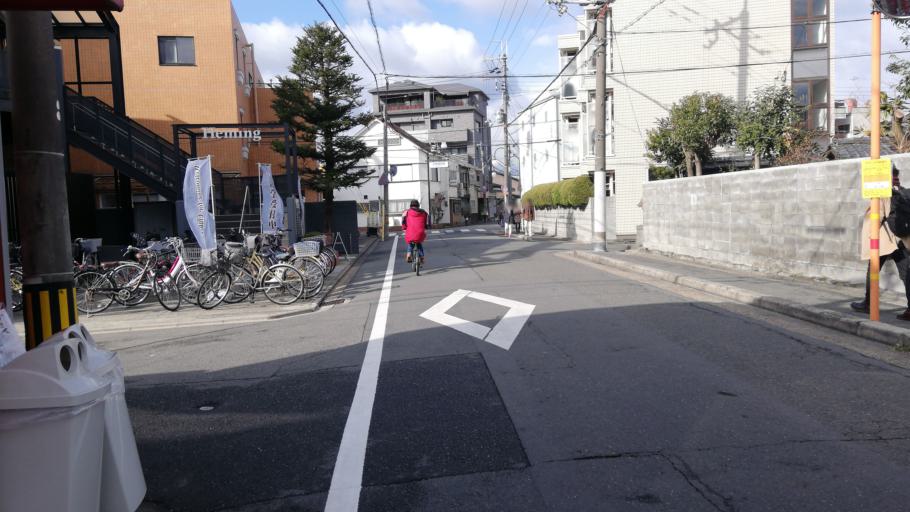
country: JP
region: Kyoto
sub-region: Kyoto-shi
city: Kamigyo-ku
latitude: 35.0300
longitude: 135.7753
